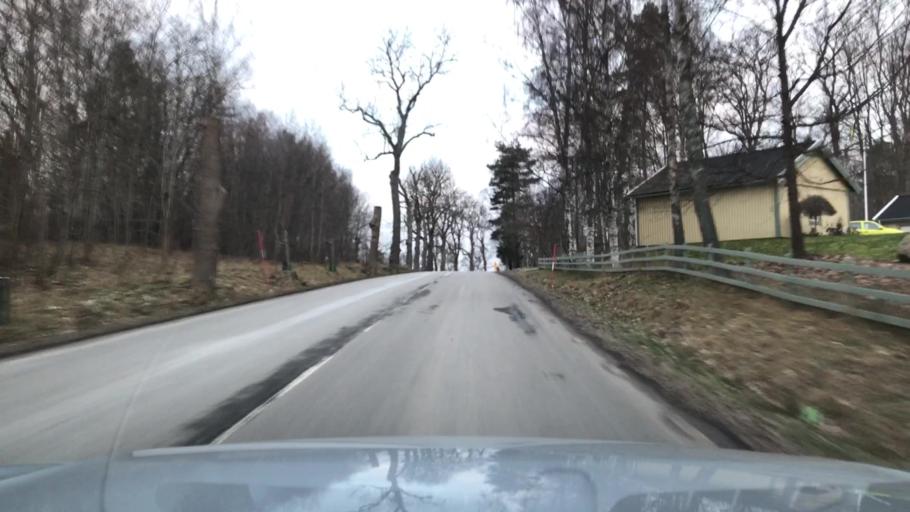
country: SE
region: OEstergoetland
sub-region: Norrkopings Kommun
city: Kimstad
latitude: 58.5168
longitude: 15.9733
